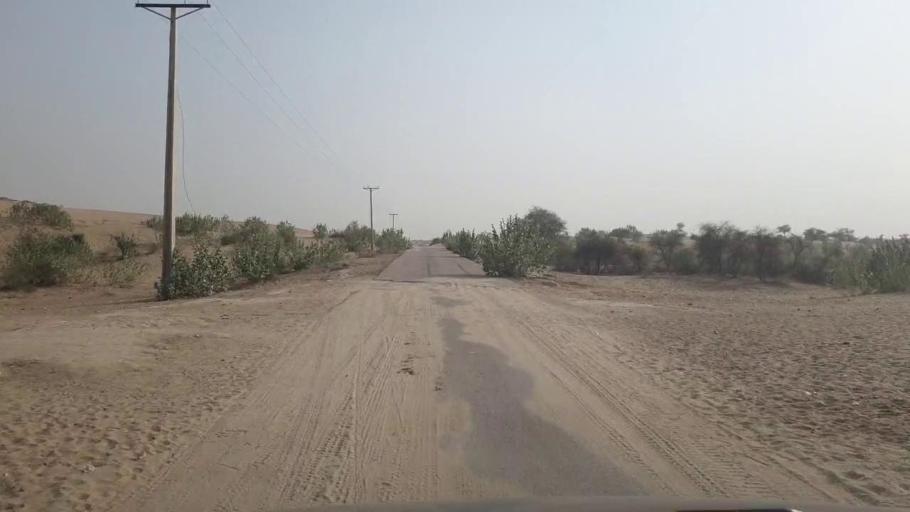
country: PK
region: Sindh
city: Chor
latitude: 25.5375
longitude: 69.9601
